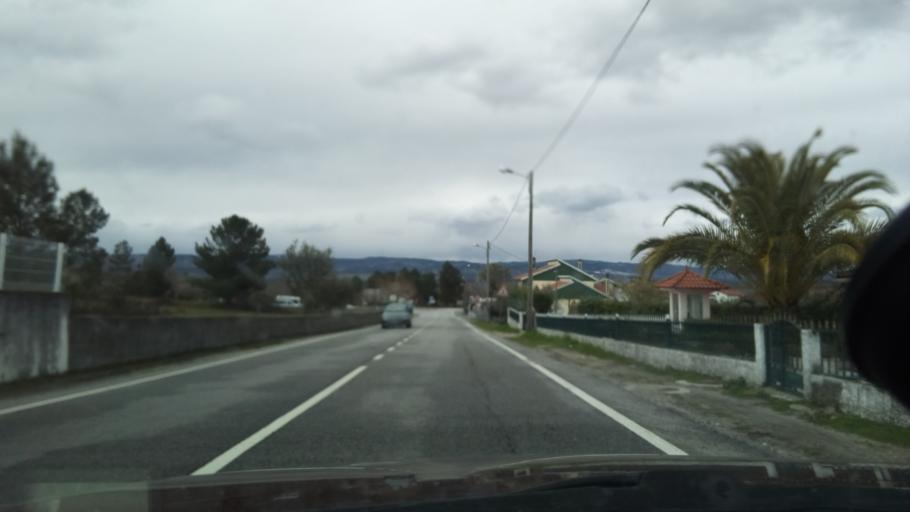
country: PT
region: Guarda
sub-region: Fornos de Algodres
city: Fornos de Algodres
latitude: 40.5287
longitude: -7.5761
